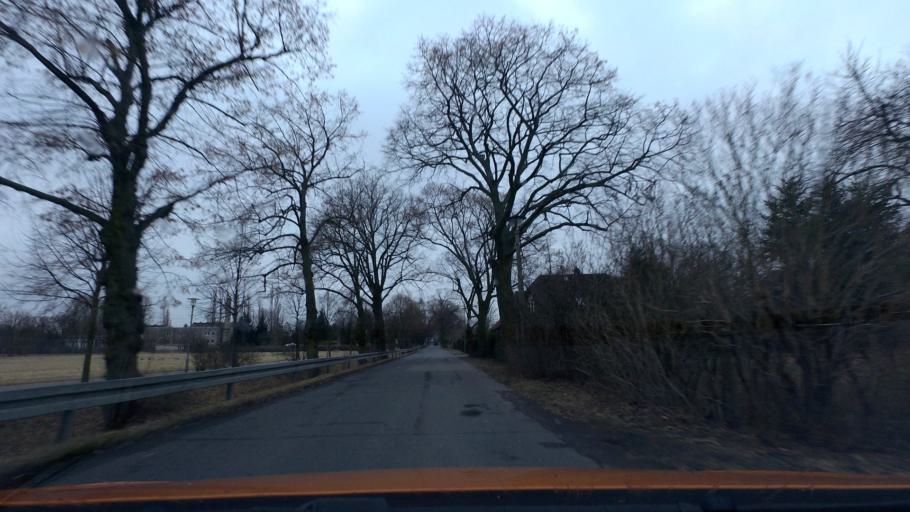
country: DE
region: Berlin
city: Falkenberg
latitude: 52.5714
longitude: 13.5456
